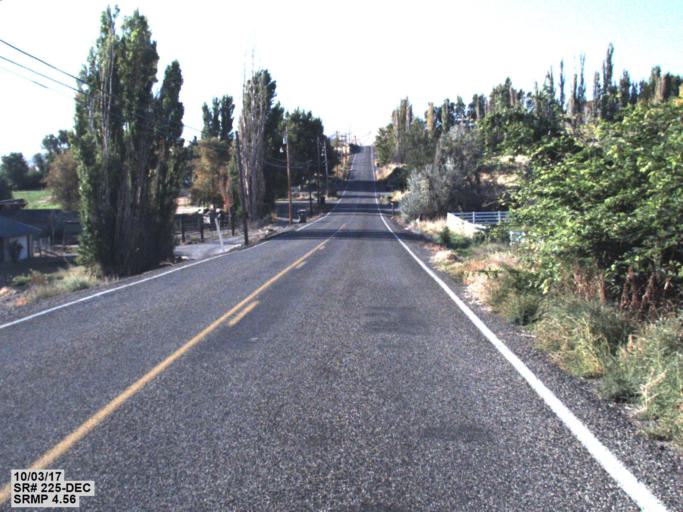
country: US
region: Washington
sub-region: Benton County
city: Benton City
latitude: 46.3093
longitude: -119.4934
